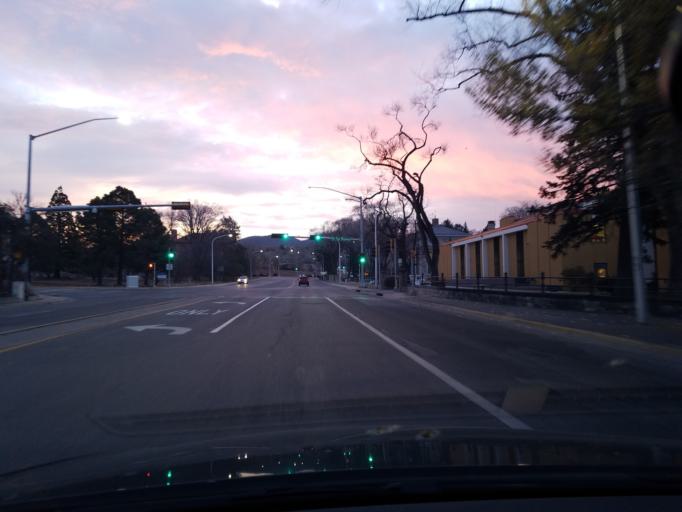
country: US
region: New Mexico
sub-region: Santa Fe County
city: Santa Fe
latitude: 35.6920
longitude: -105.9392
